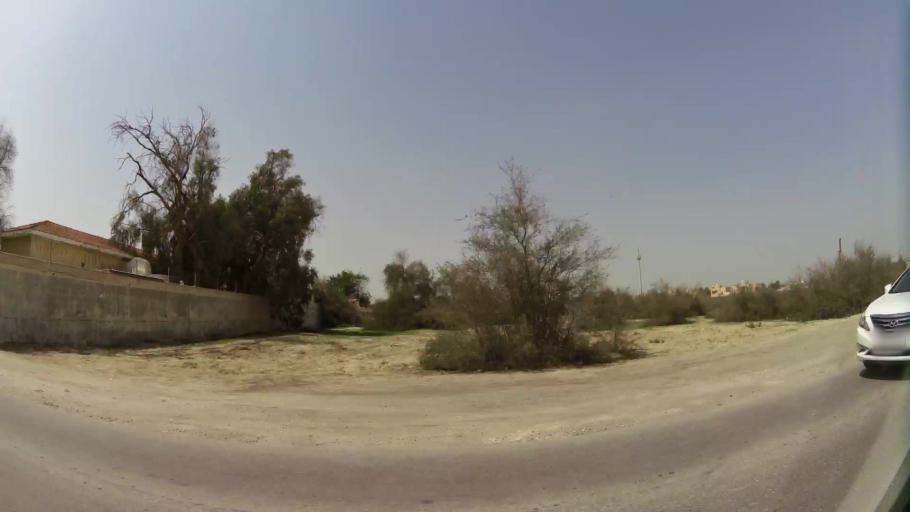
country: BH
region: Manama
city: Jidd Hafs
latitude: 26.2206
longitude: 50.4782
